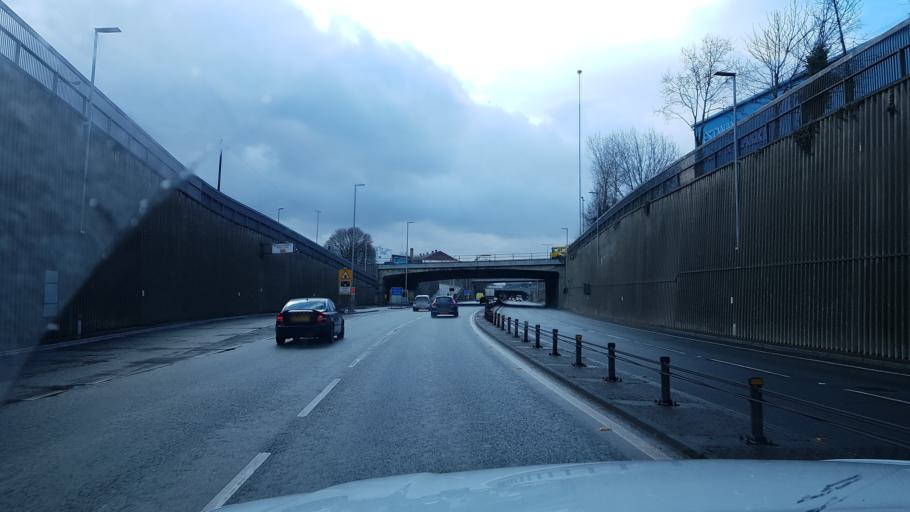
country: GB
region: England
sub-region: Liverpool
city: Liverpool
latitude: 53.4168
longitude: -2.9798
